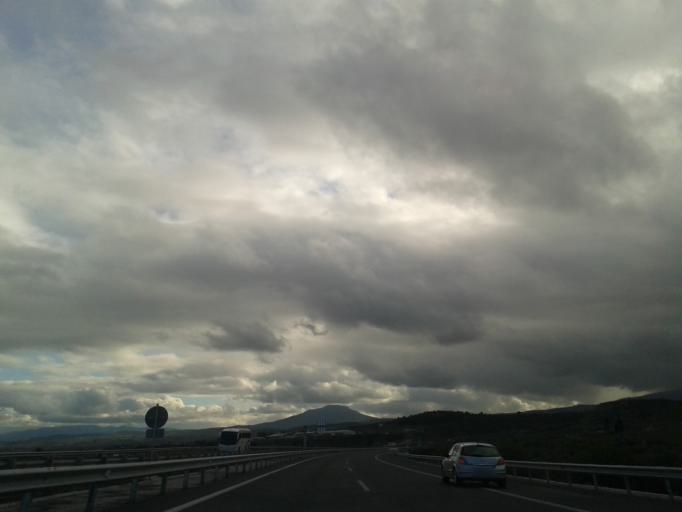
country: GR
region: Peloponnese
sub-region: Nomos Korinthias
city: Moulki
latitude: 37.9898
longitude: 22.7358
